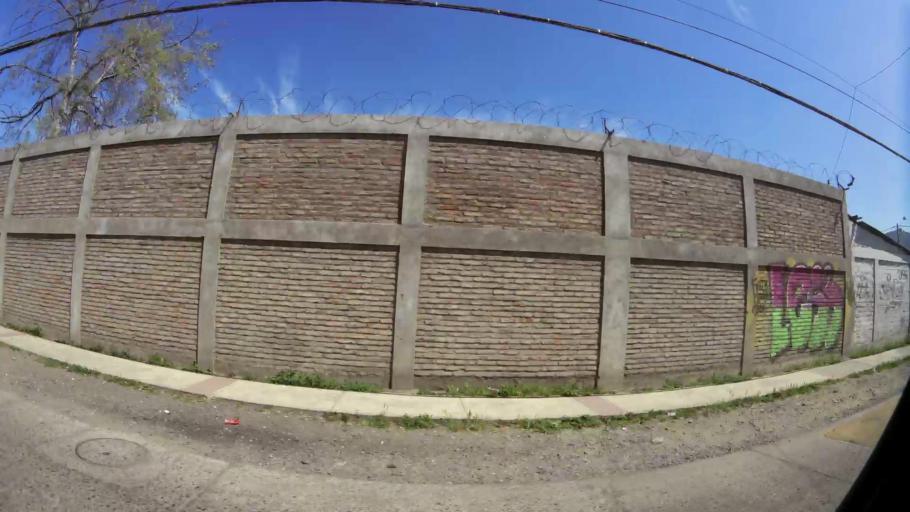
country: CL
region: Santiago Metropolitan
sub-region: Provincia de Talagante
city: Talagante
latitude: -33.6548
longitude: -70.9255
